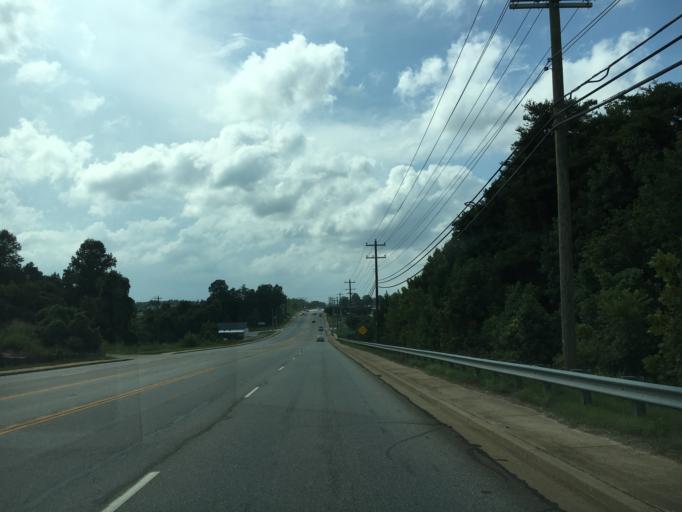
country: US
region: South Carolina
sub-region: Cherokee County
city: Gaffney
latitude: 35.0690
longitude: -81.6737
